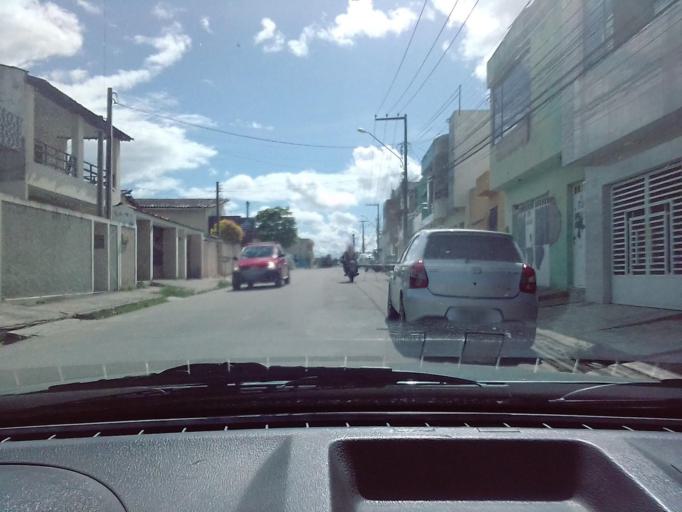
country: BR
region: Pernambuco
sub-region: Vitoria De Santo Antao
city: Vitoria de Santo Antao
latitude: -8.1180
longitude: -35.3083
